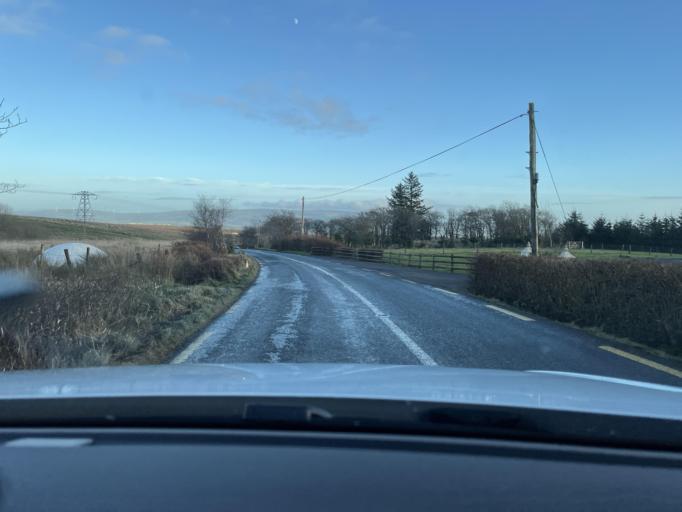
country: IE
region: Ulster
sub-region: An Cabhan
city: Ballyconnell
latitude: 54.1658
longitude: -7.7982
